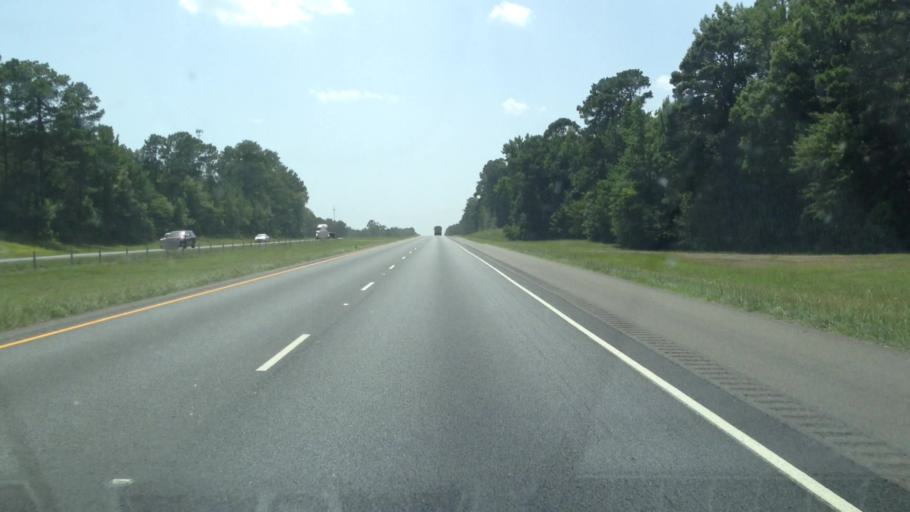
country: US
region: Louisiana
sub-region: Bienville Parish
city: Arcadia
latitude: 32.5630
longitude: -93.1055
